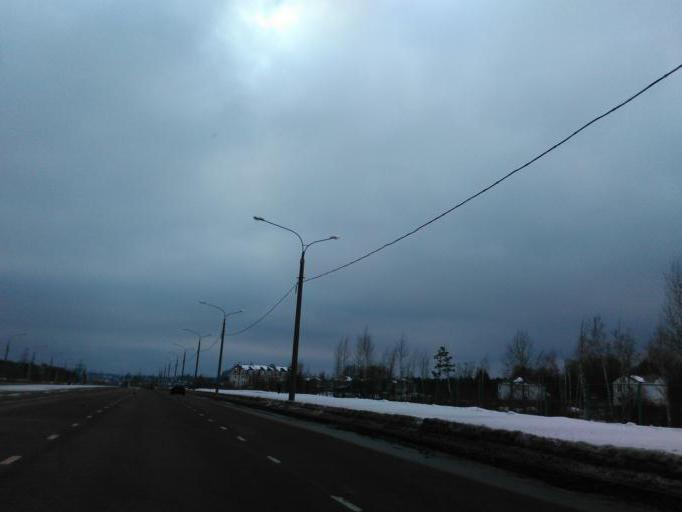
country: RU
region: Moscow
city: Zelenograd
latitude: 55.9627
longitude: 37.1859
